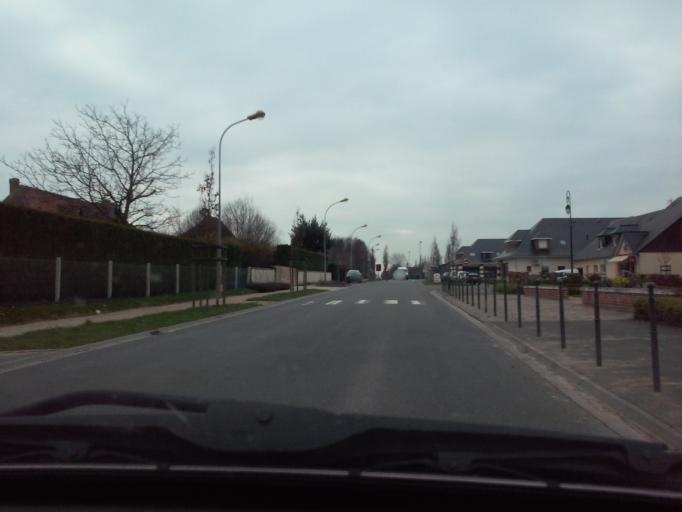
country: FR
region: Haute-Normandie
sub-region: Departement de la Seine-Maritime
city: Saint-Arnoult
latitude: 49.5280
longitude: 0.6669
